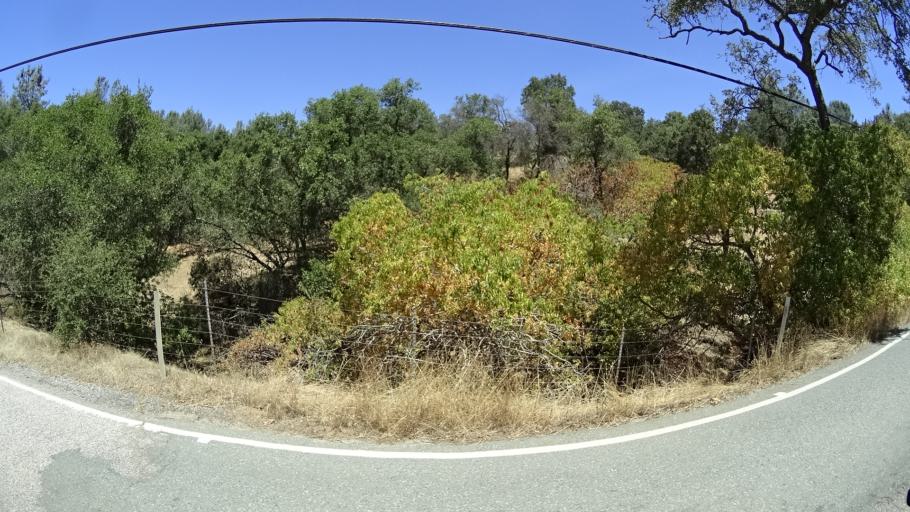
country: US
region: California
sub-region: Calaveras County
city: Valley Springs
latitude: 38.2291
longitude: -120.8516
